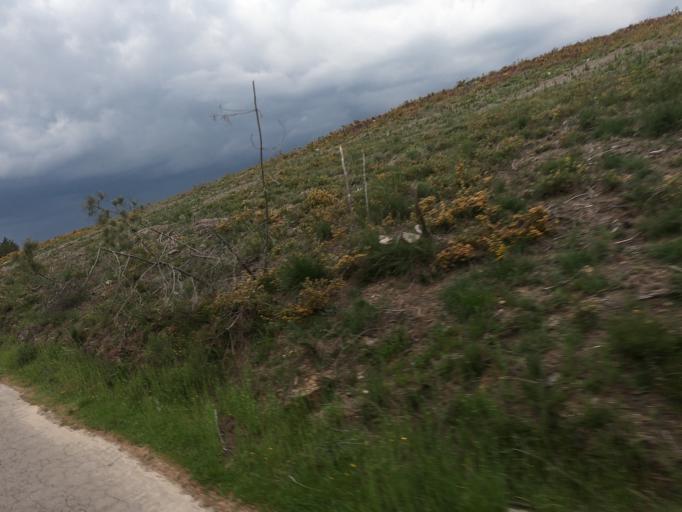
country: PT
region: Vila Real
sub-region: Sabrosa
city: Vilela
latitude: 41.2391
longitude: -7.6690
